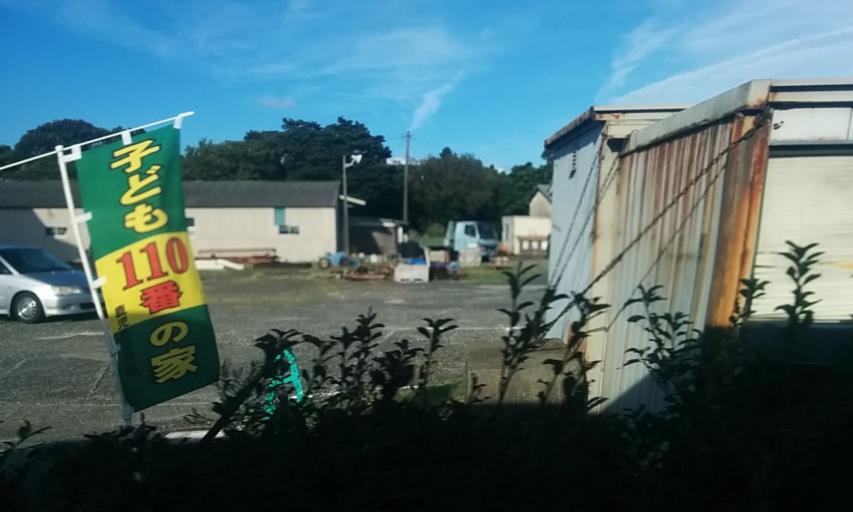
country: JP
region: Kagoshima
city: Nishinoomote
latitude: 30.3812
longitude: 130.6604
